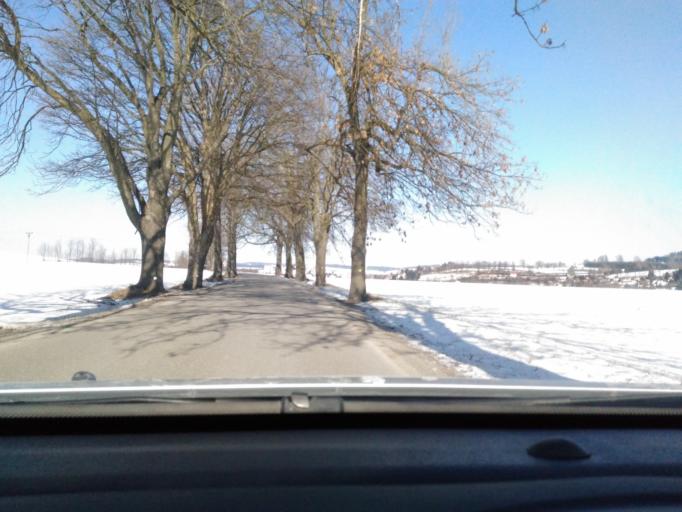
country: CZ
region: Vysocina
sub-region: Okres Zd'ar nad Sazavou
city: Nove Mesto na Morave
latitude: 49.5488
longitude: 16.0681
